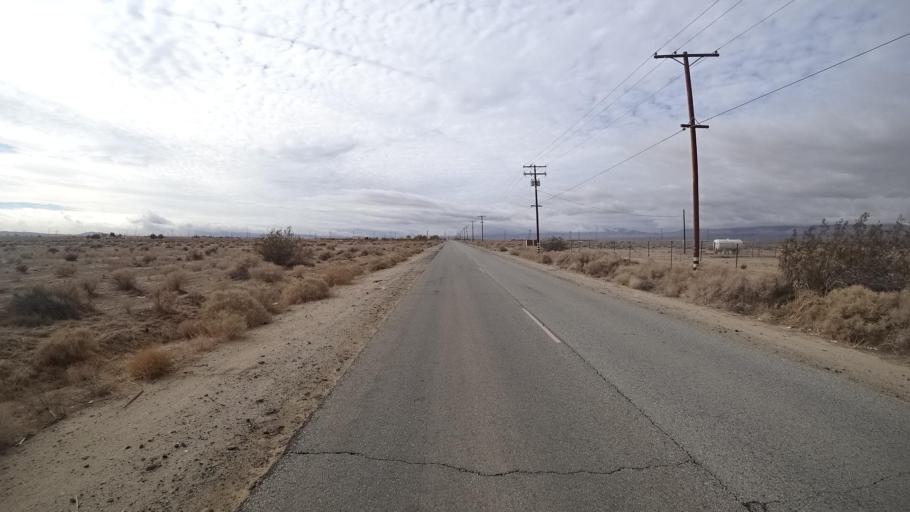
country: US
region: California
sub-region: Kern County
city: Rosamond
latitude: 34.8636
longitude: -118.2948
